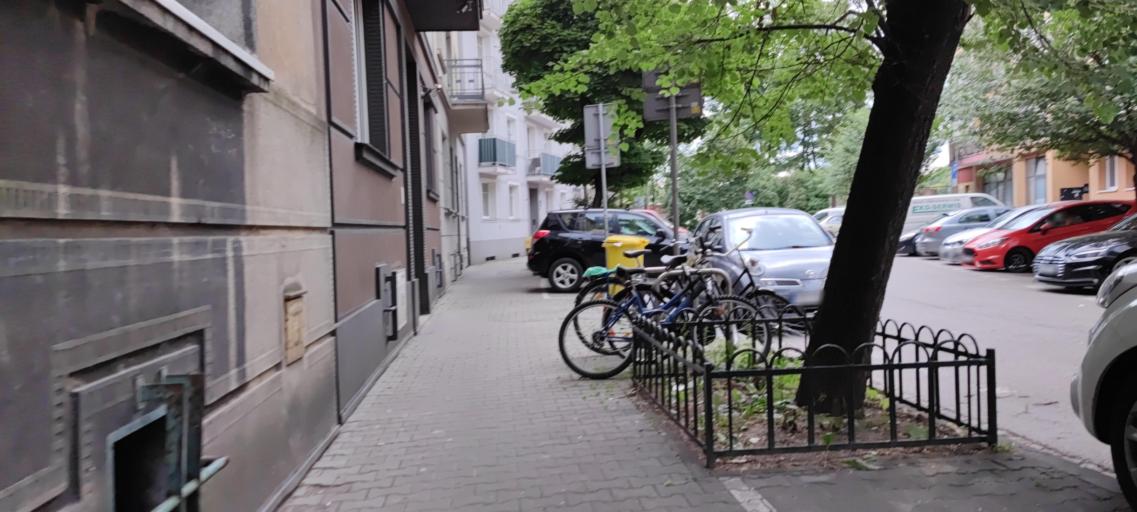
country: PL
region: Lesser Poland Voivodeship
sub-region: Krakow
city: Krakow
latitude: 50.0566
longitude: 19.9194
